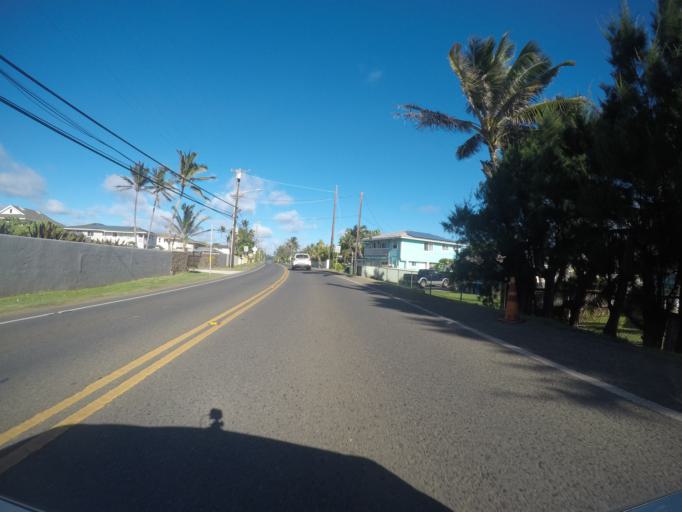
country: US
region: Hawaii
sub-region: Honolulu County
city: La'ie
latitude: 21.6519
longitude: -157.9283
